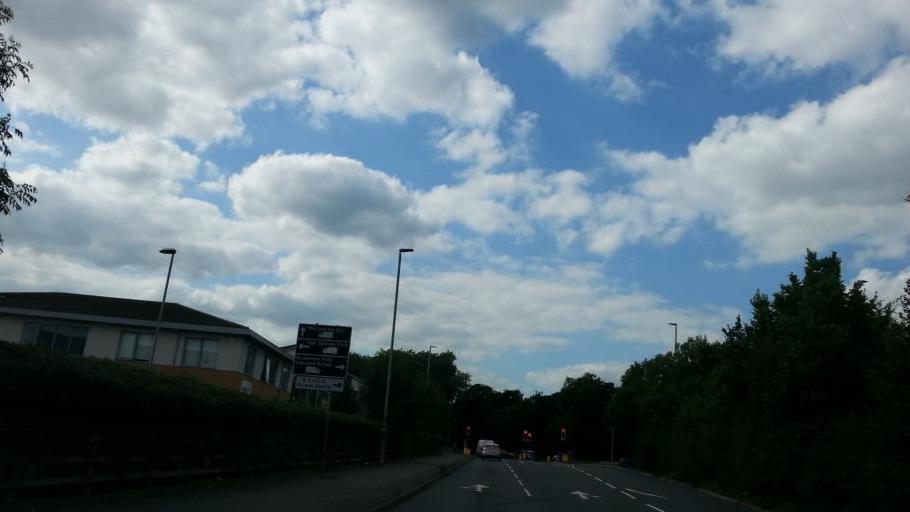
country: GB
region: England
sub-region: Leicestershire
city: Kirby Muxloe
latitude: 52.6297
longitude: -1.2071
